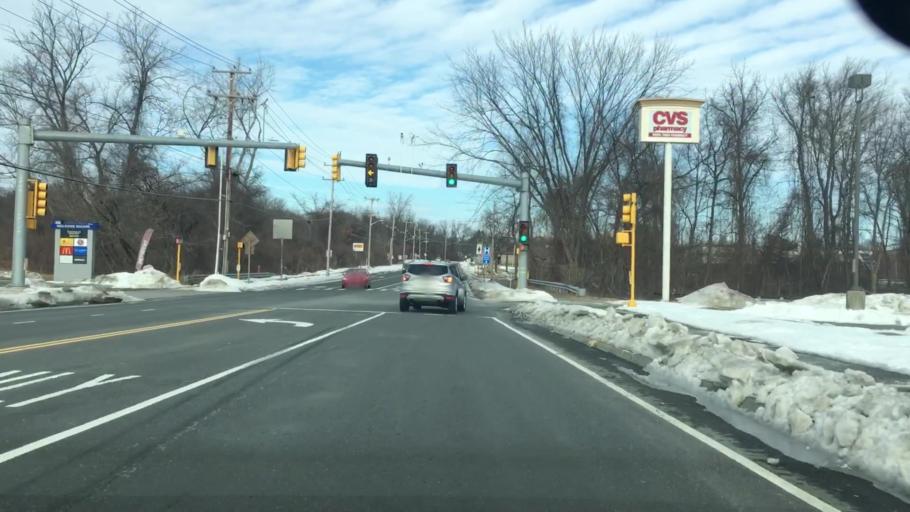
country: US
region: Massachusetts
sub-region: Hampden County
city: Holyoke
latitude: 42.1751
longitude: -72.6403
